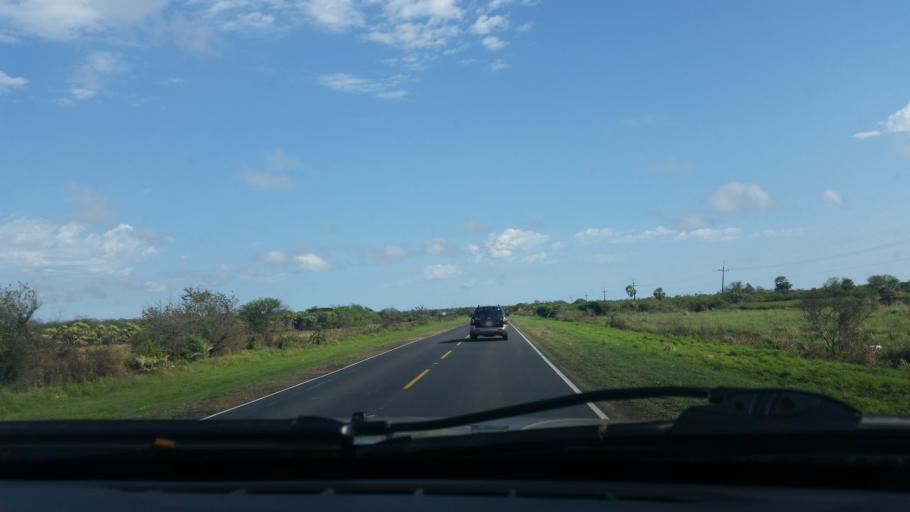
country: PY
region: Presidente Hayes
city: Benjamin Aceval
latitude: -24.9268
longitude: -57.5683
